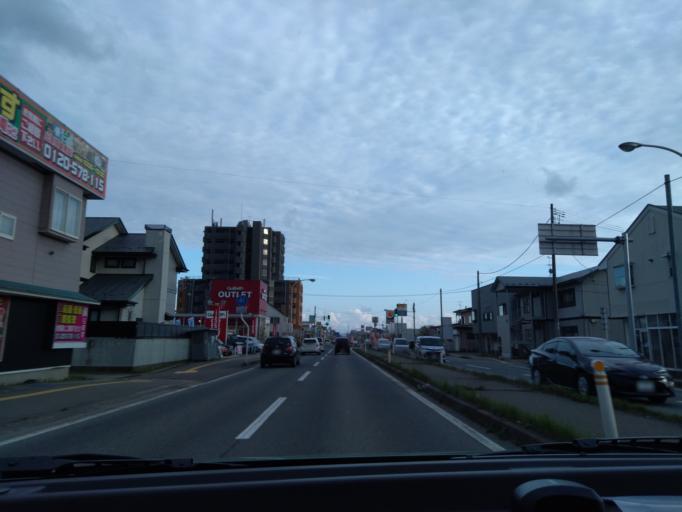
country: JP
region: Akita
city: Akita
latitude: 39.7248
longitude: 140.1481
